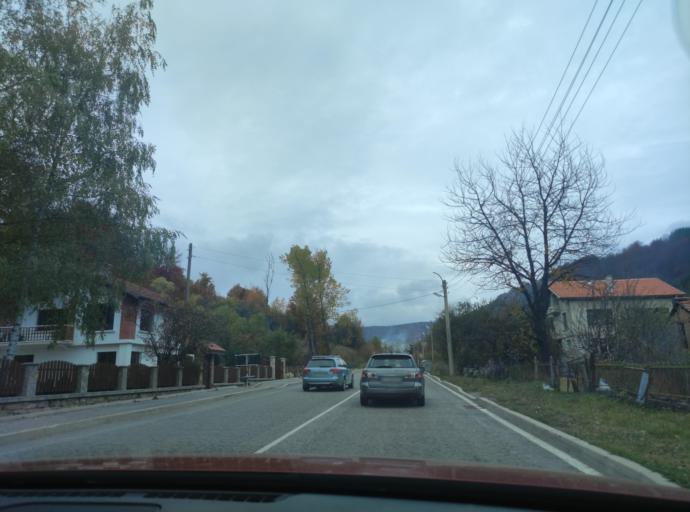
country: BG
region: Sofiya
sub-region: Obshtina Godech
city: Godech
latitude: 43.0838
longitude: 23.1032
